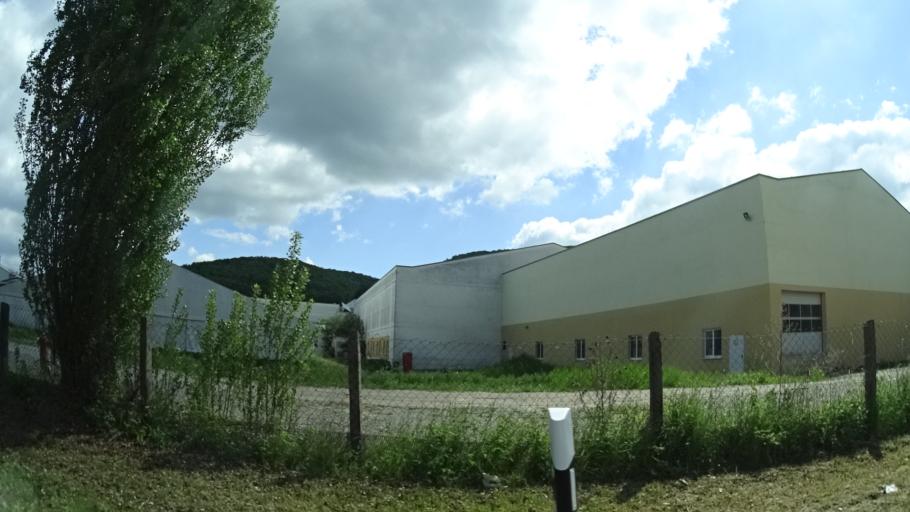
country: DE
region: Thuringia
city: Ritschenhausen
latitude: 50.5187
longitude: 10.4293
